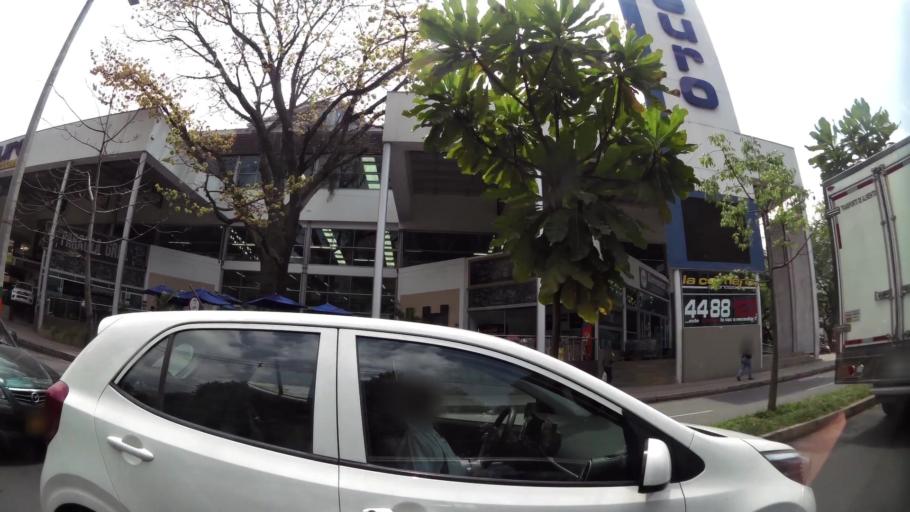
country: CO
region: Antioquia
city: Envigado
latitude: 6.1836
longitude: -75.5793
